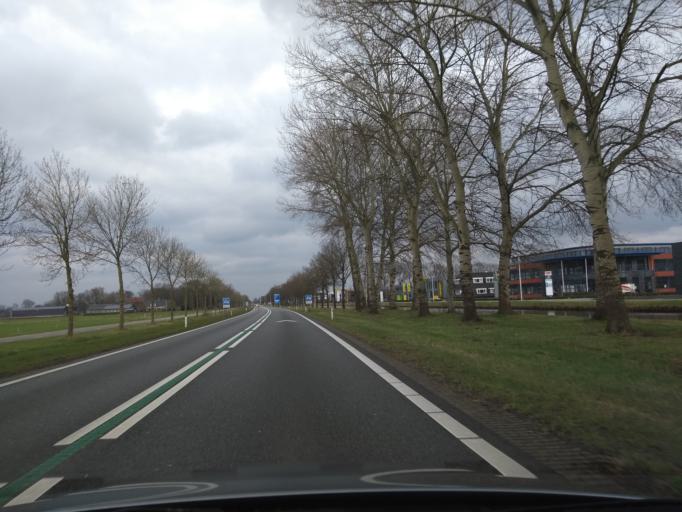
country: NL
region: Overijssel
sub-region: Gemeente Staphorst
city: Staphorst
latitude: 52.5899
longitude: 6.2413
